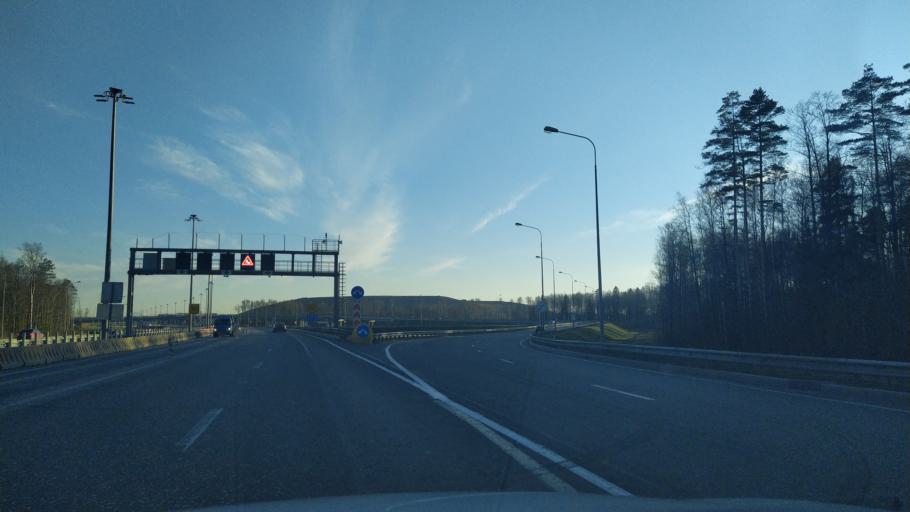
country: RU
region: St.-Petersburg
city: Levashovo
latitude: 60.0786
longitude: 30.1865
